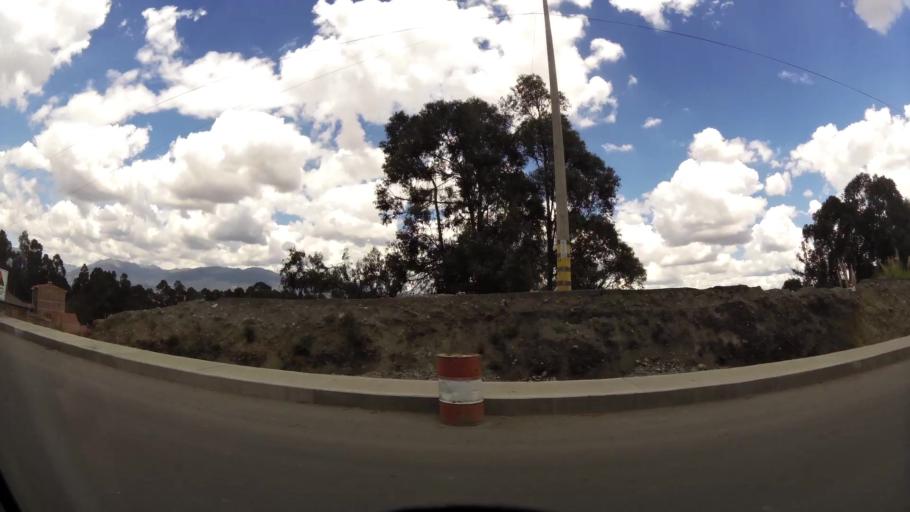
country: EC
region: Azuay
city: Cuenca
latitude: -2.9195
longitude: -79.0049
